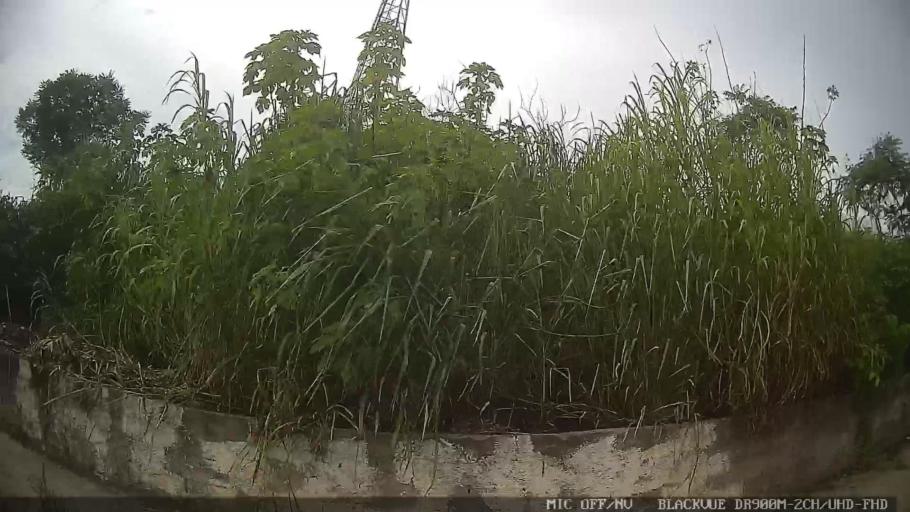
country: BR
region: Sao Paulo
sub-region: Aruja
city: Aruja
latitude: -23.4416
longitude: -46.2790
